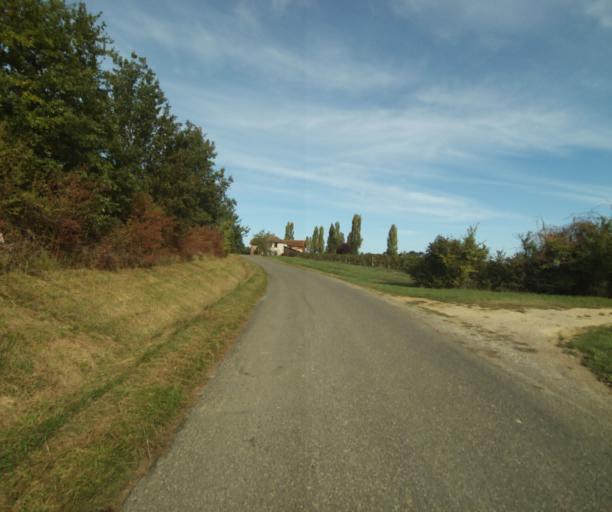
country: FR
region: Midi-Pyrenees
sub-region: Departement du Gers
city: Eauze
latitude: 43.9070
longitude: 0.1420
